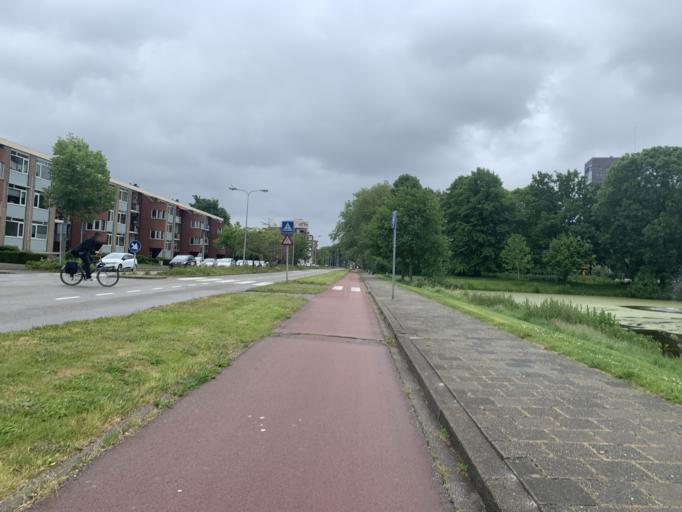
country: NL
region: Groningen
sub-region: Gemeente Groningen
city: Groningen
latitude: 53.2279
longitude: 6.5434
